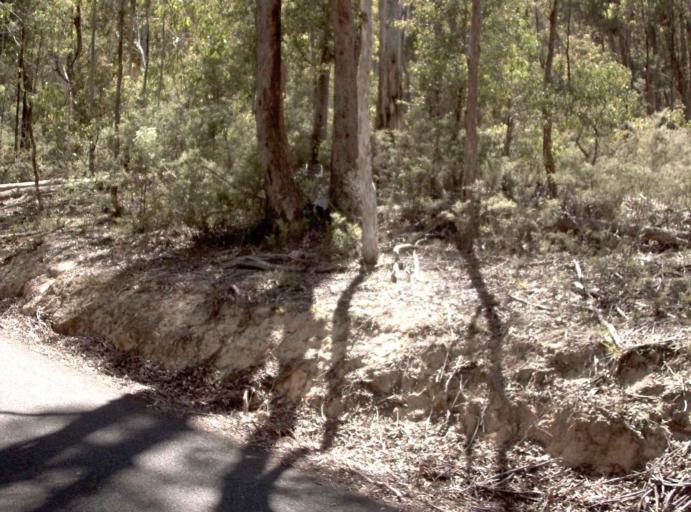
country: AU
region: New South Wales
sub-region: Bombala
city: Bombala
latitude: -37.1133
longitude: 148.7554
